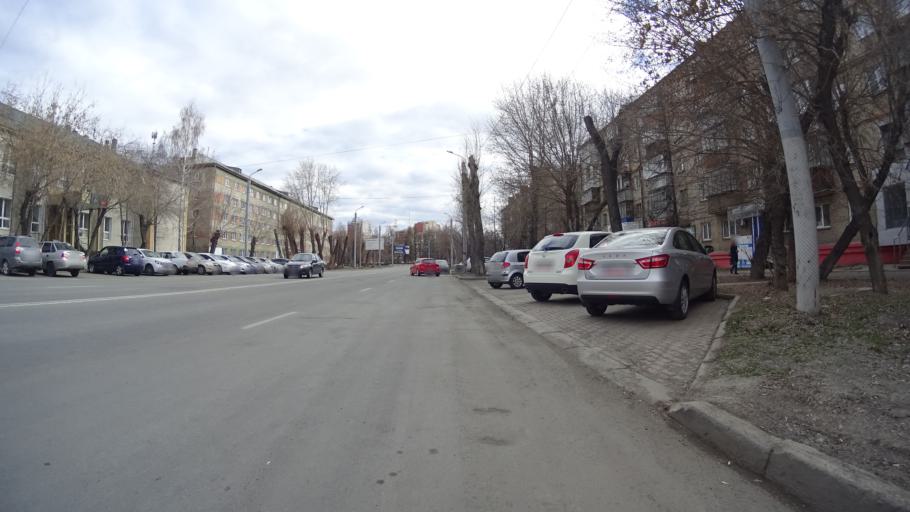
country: RU
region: Chelyabinsk
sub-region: Gorod Chelyabinsk
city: Chelyabinsk
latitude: 55.1506
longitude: 61.3803
